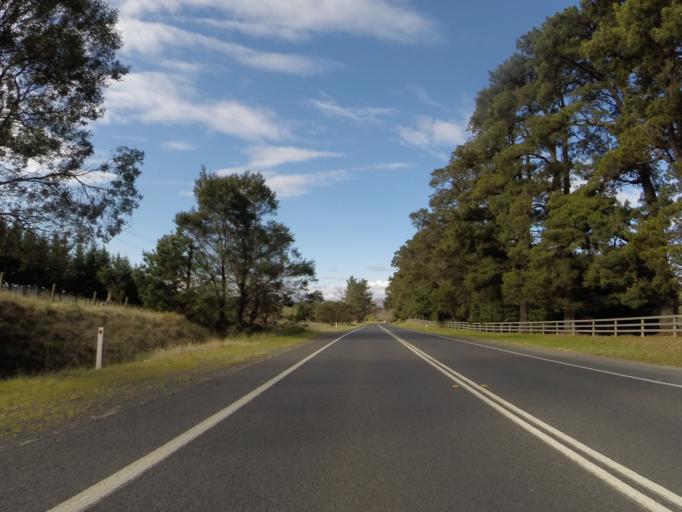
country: AU
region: New South Wales
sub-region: Wingecarribee
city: Bundanoon
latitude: -34.5830
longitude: 150.2982
